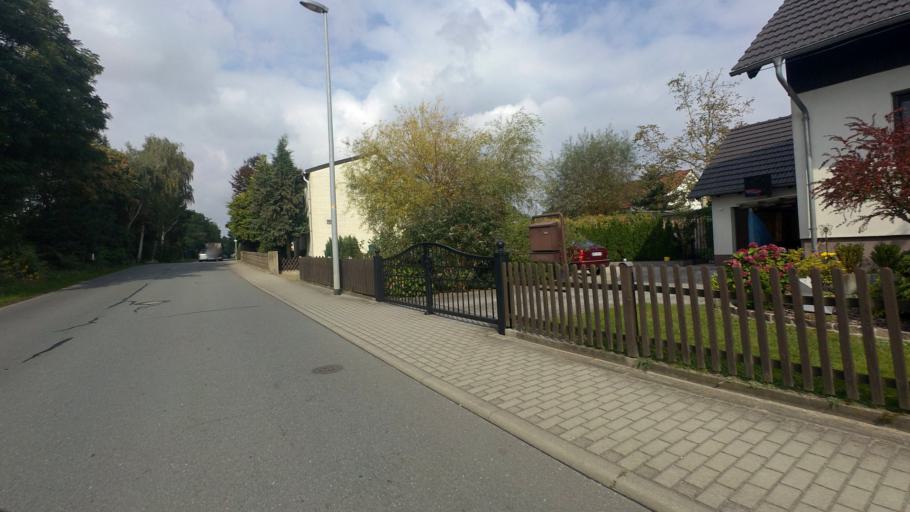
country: DE
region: Brandenburg
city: Bad Liebenwerda
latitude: 51.5183
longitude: 13.4170
